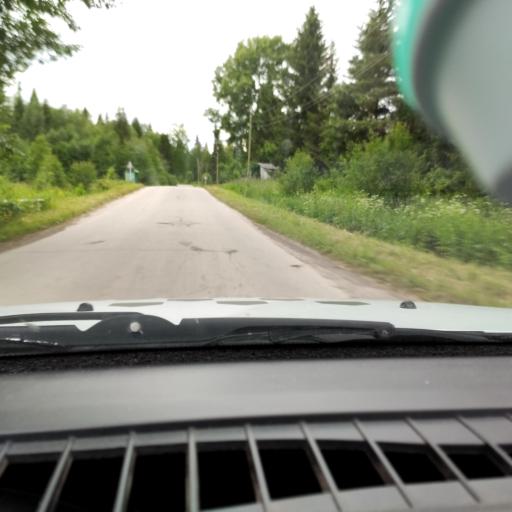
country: RU
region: Perm
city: Lys'va
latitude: 58.1172
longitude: 57.6967
